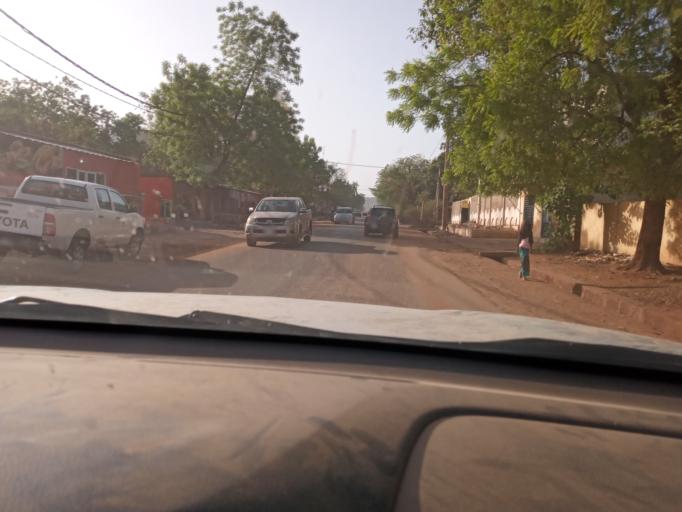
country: ML
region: Bamako
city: Bamako
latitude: 12.6612
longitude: -7.9724
